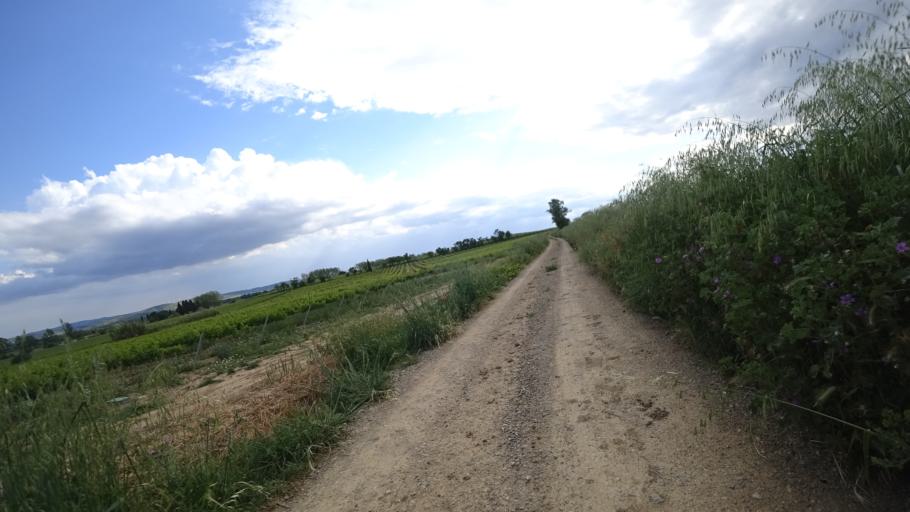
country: FR
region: Languedoc-Roussillon
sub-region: Departement de l'Aude
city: Ginestas
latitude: 43.2544
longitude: 2.8788
